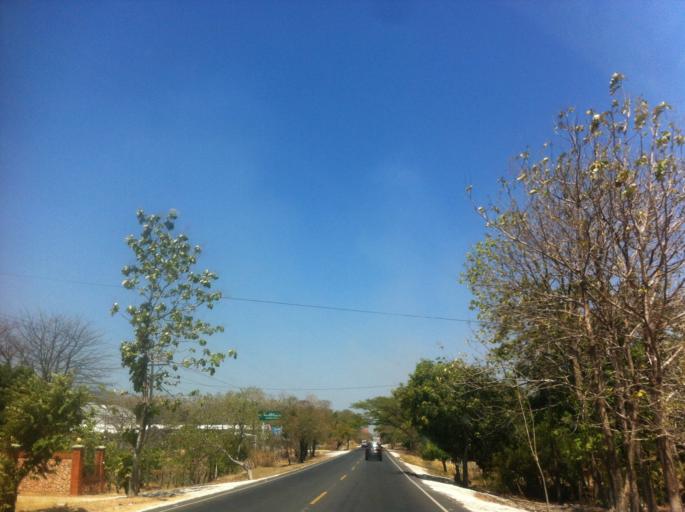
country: CR
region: Guanacaste
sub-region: Canton de Nicoya
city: Nicoya
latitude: 10.1964
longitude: -85.4826
